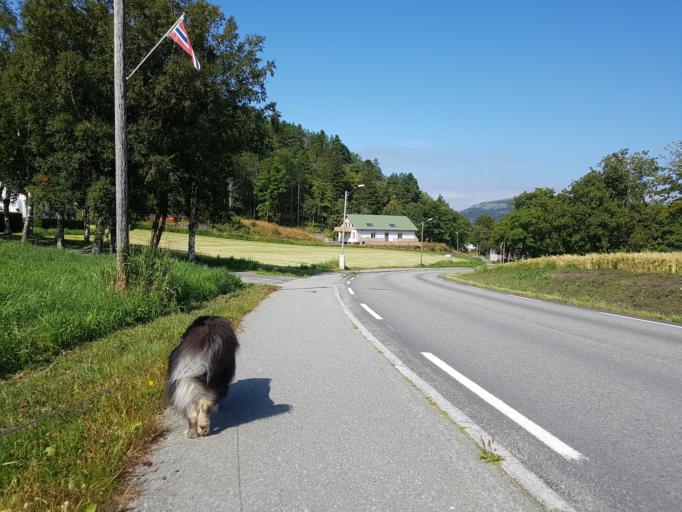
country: NO
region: Sor-Trondelag
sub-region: Agdenes
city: Lensvik
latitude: 63.6293
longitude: 9.8249
